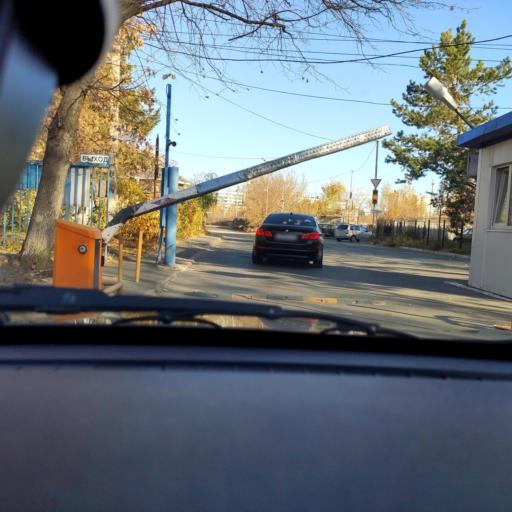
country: RU
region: Samara
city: Tol'yatti
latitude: 53.5232
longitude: 49.3295
